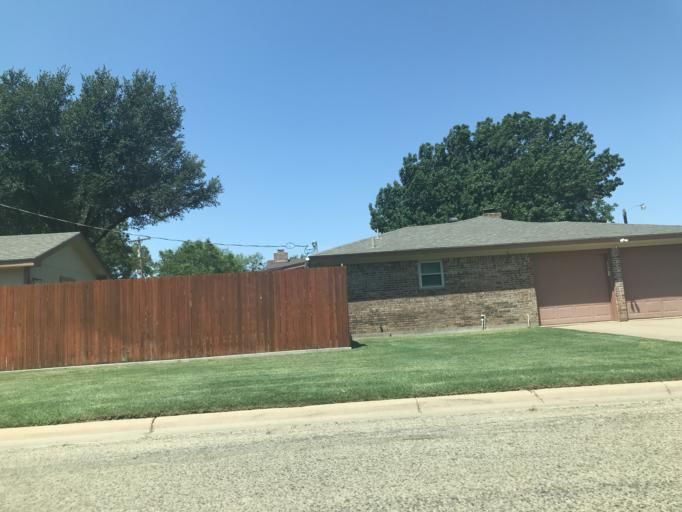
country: US
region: Texas
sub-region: Taylor County
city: Abilene
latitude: 32.4576
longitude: -99.7003
